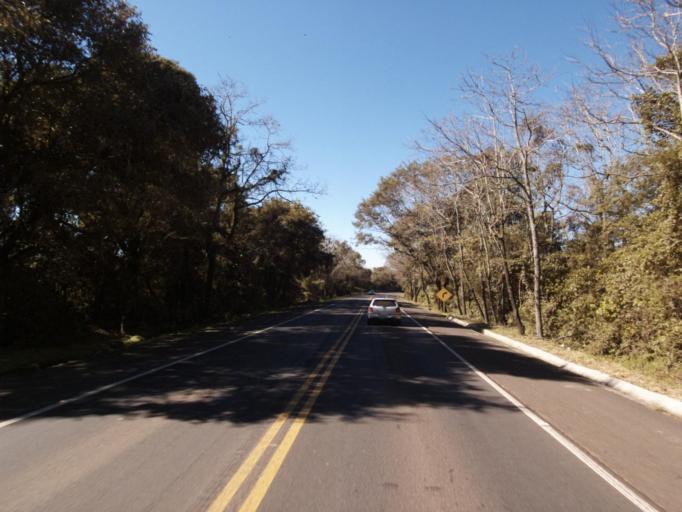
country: BR
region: Santa Catarina
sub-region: Chapeco
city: Chapeco
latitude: -26.8987
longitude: -52.8777
